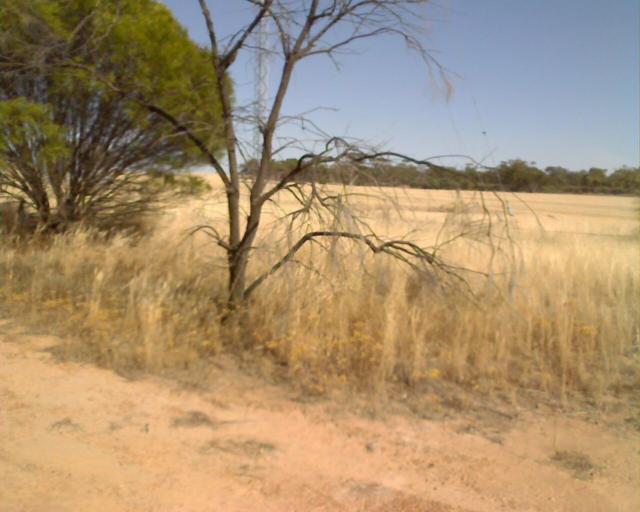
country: AU
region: Western Australia
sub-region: Merredin
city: Merredin
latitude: -31.4251
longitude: 117.7504
